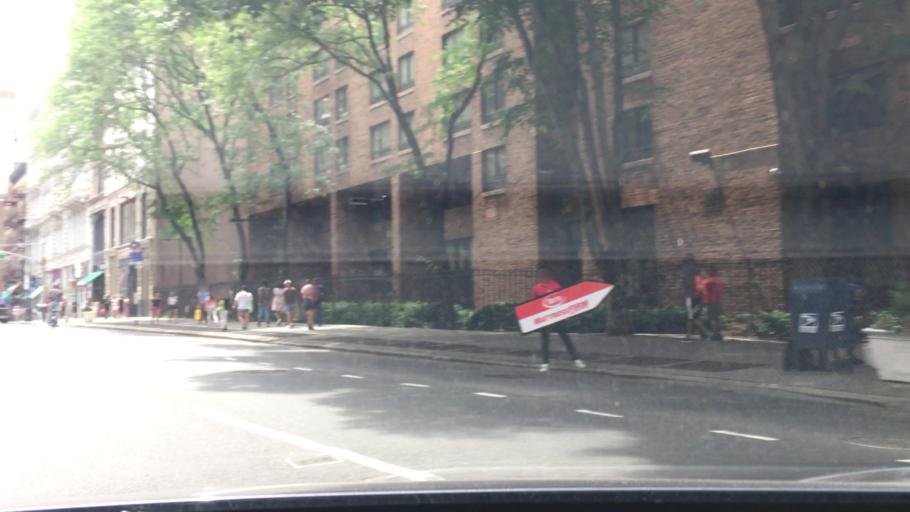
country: US
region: New York
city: New York City
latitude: 40.7278
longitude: -73.9948
